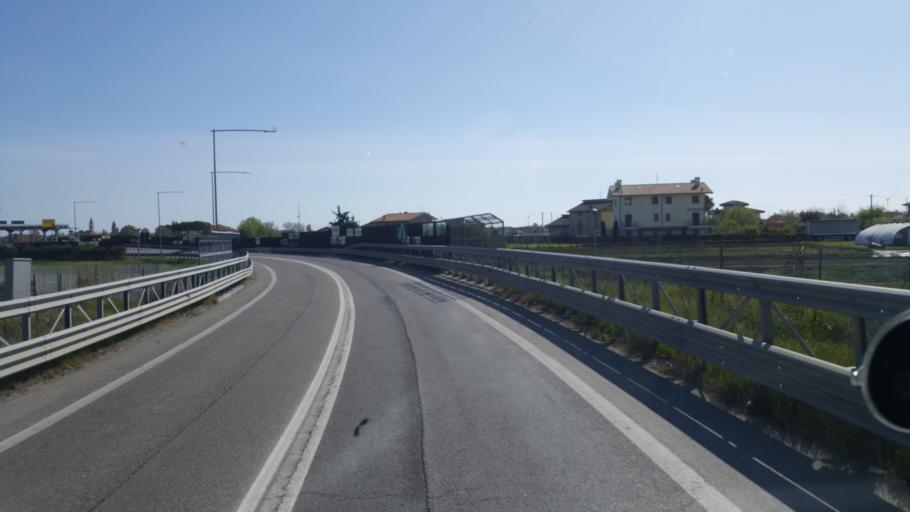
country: IT
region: Emilia-Romagna
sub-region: Forli-Cesena
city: Gatteo-Sant'Angelo
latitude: 44.1156
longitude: 12.3874
